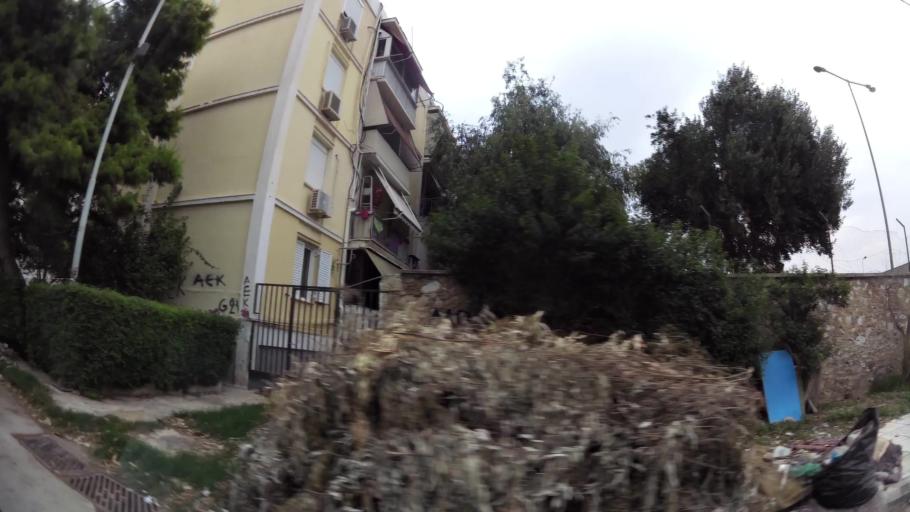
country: GR
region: Attica
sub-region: Nomos Piraios
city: Agios Ioannis Rentis
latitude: 37.9726
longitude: 23.6668
